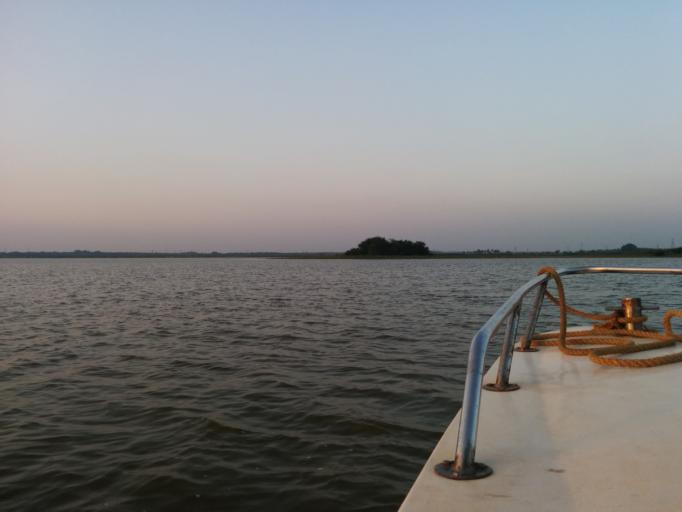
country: IN
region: Tamil Nadu
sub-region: Villupuram
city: Auroville
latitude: 11.9537
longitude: 79.7485
